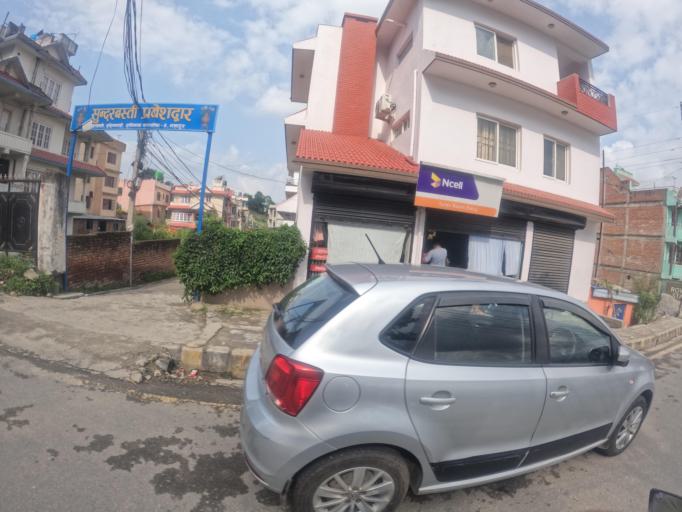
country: NP
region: Central Region
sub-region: Bagmati Zone
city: Bhaktapur
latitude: 27.6668
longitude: 85.3862
